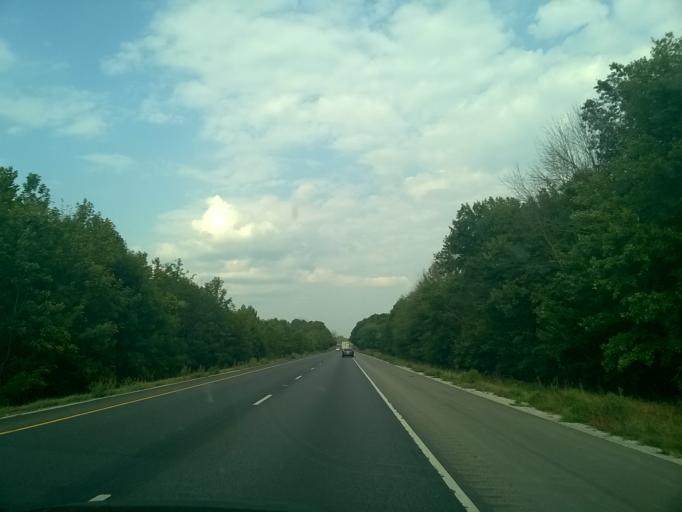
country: US
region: Indiana
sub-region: Clay County
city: Brazil
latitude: 39.4596
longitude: -87.0835
